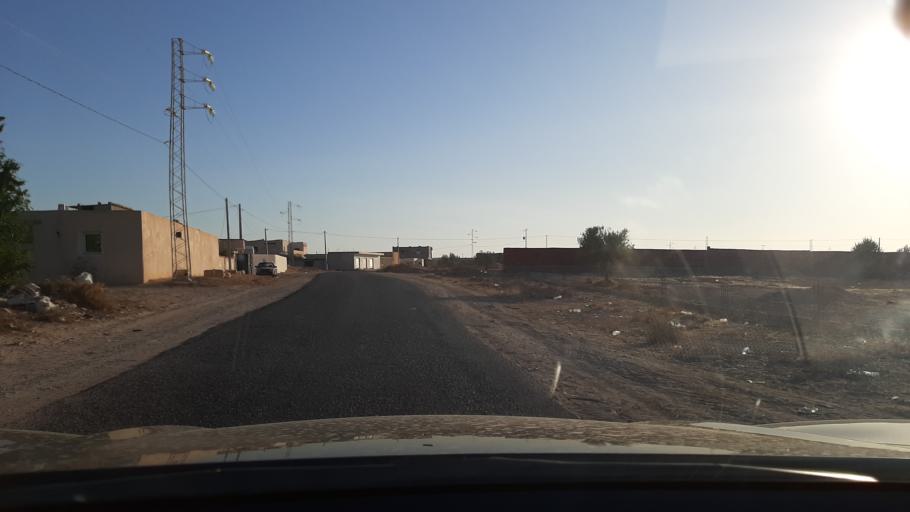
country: TN
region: Qabis
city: Matmata
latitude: 33.6168
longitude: 10.2492
